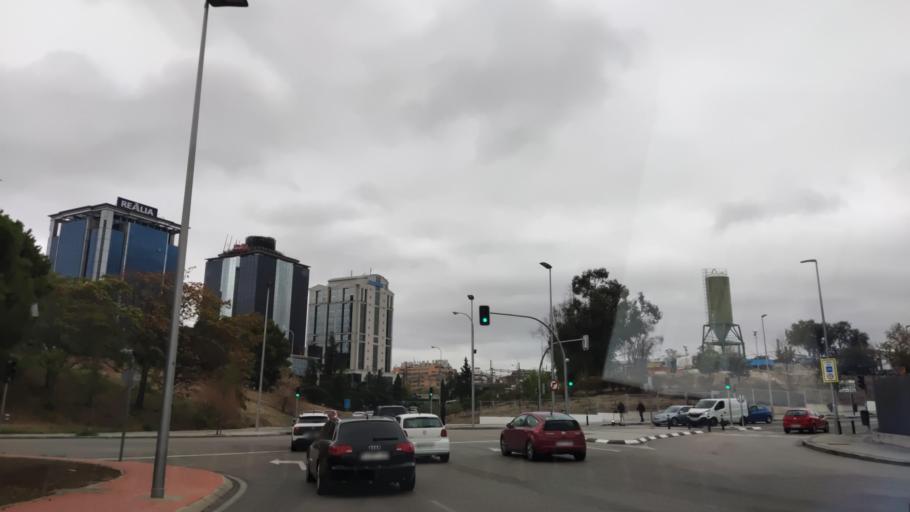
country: ES
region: Madrid
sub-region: Provincia de Madrid
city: Puente de Vallecas
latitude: 40.3906
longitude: -3.6754
